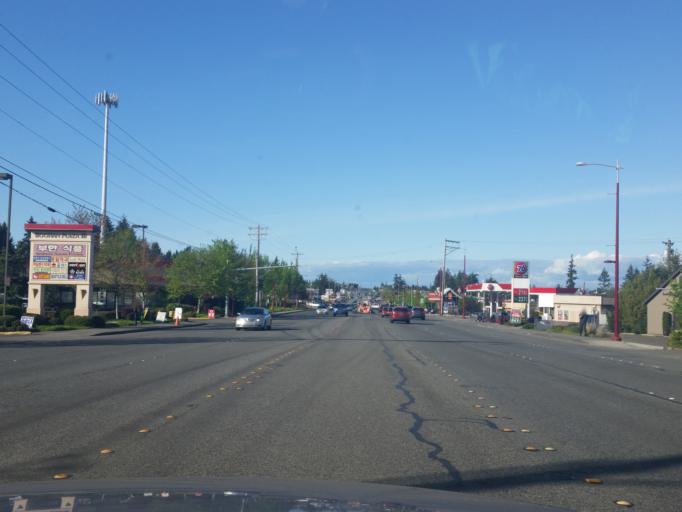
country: US
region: Washington
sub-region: Snohomish County
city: Esperance
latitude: 47.7928
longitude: -122.3367
